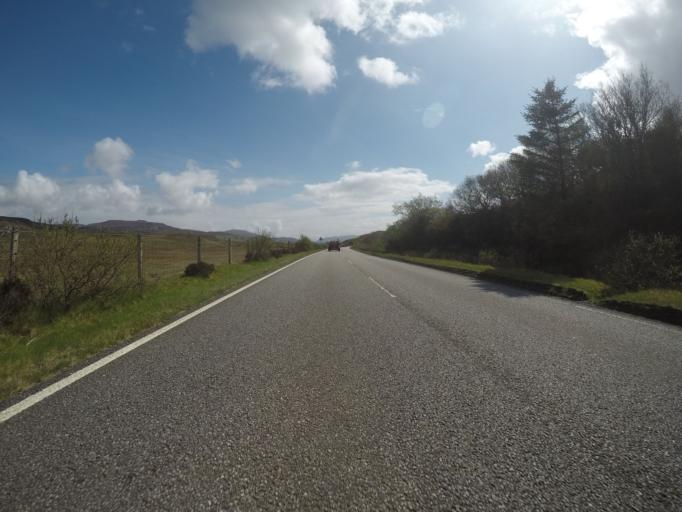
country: GB
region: Scotland
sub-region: Highland
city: Isle of Skye
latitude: 57.5082
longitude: -6.3371
